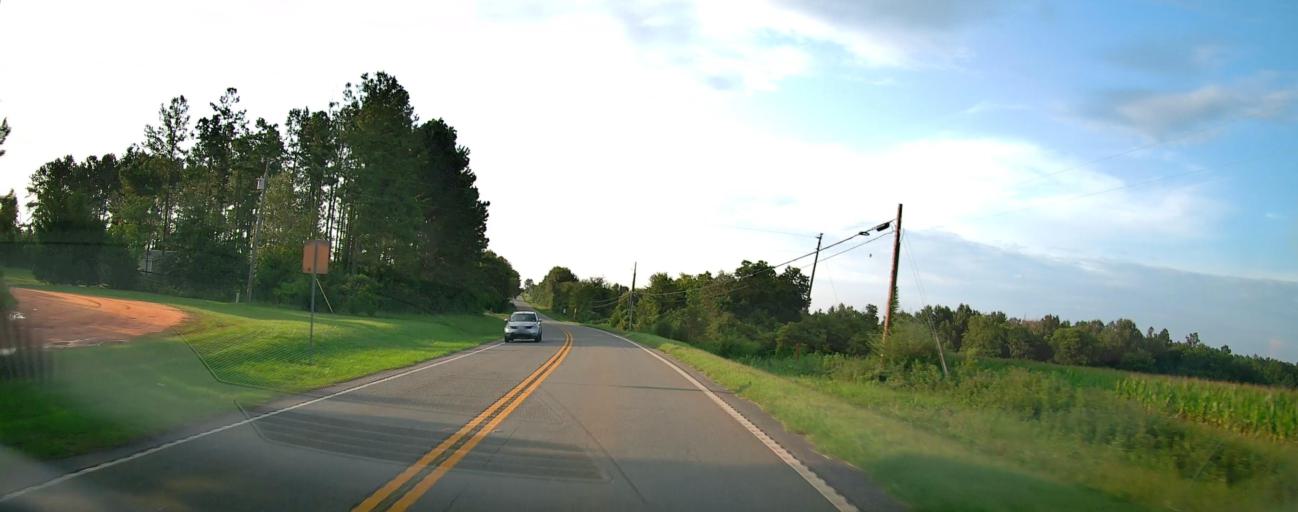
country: US
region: Georgia
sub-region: Taylor County
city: Reynolds
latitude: 32.5876
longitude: -84.0897
